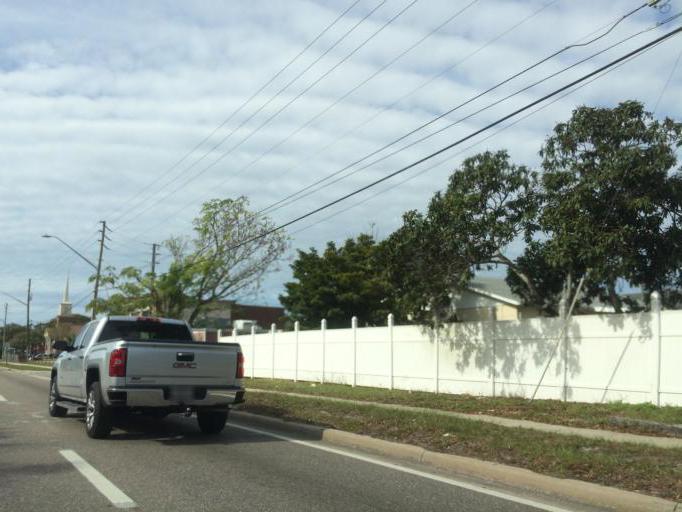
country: US
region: Florida
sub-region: Pinellas County
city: West and East Lealman
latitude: 27.8065
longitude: -82.6902
